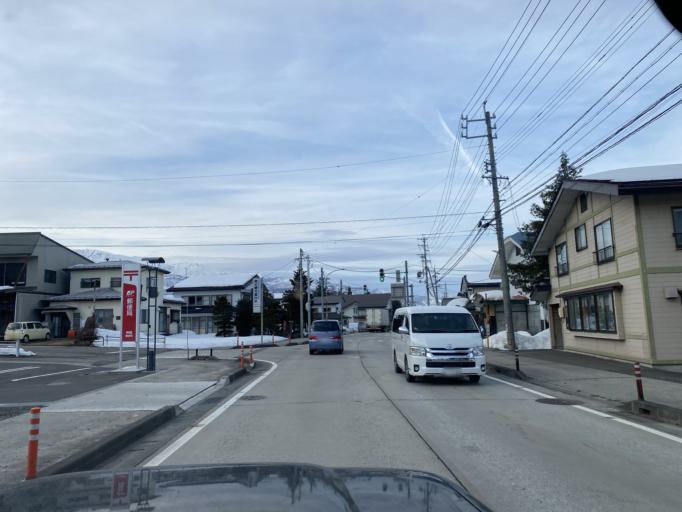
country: JP
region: Nagano
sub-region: Kitaazumi Gun
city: Hakuba
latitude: 36.6575
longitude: 137.8481
